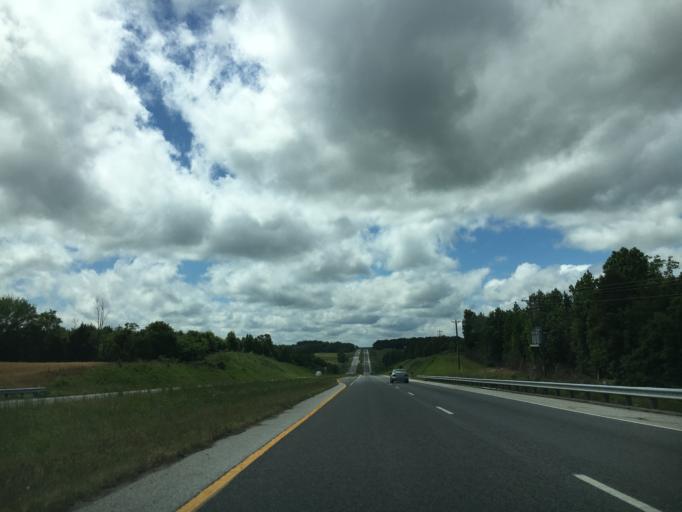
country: US
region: Virginia
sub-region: Mecklenburg County
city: Boydton
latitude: 36.6715
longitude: -78.2649
